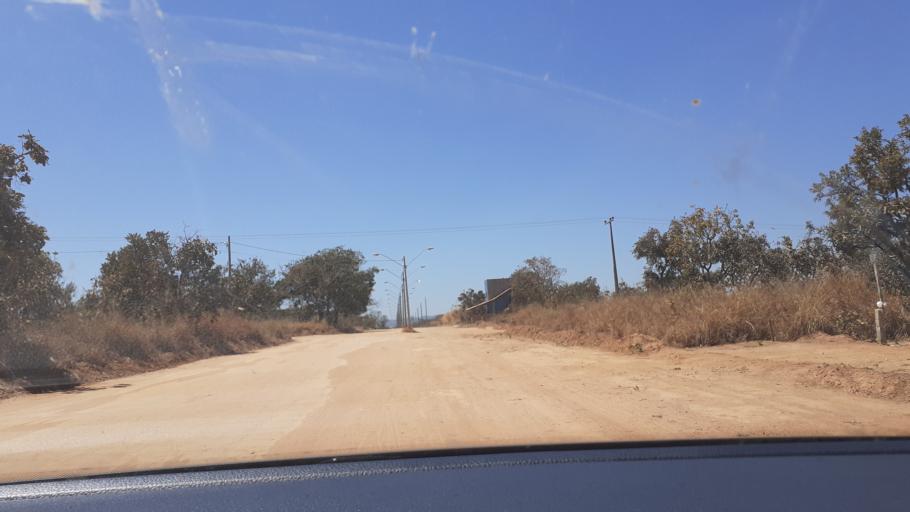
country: BR
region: Goias
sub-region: Caldas Novas
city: Caldas Novas
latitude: -17.7449
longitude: -48.6504
